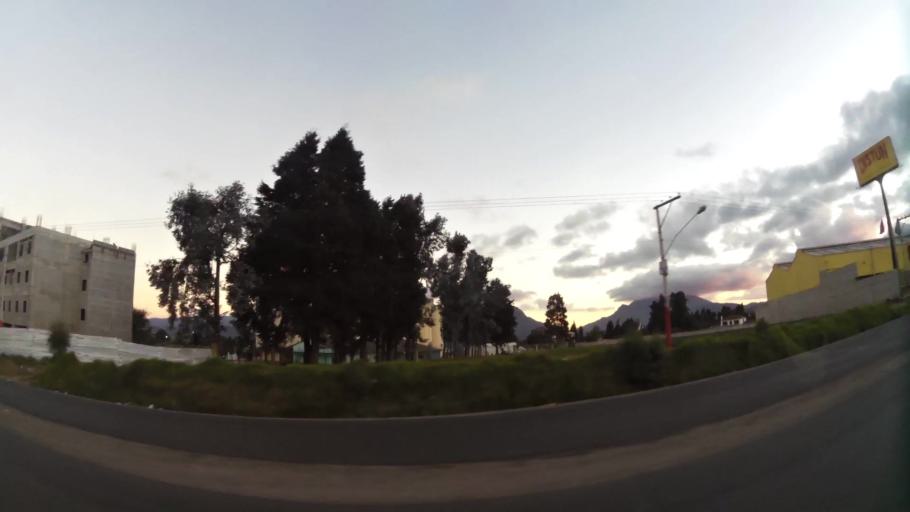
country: GT
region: Quetzaltenango
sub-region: Municipio de La Esperanza
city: La Esperanza
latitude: 14.8620
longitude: -91.5421
